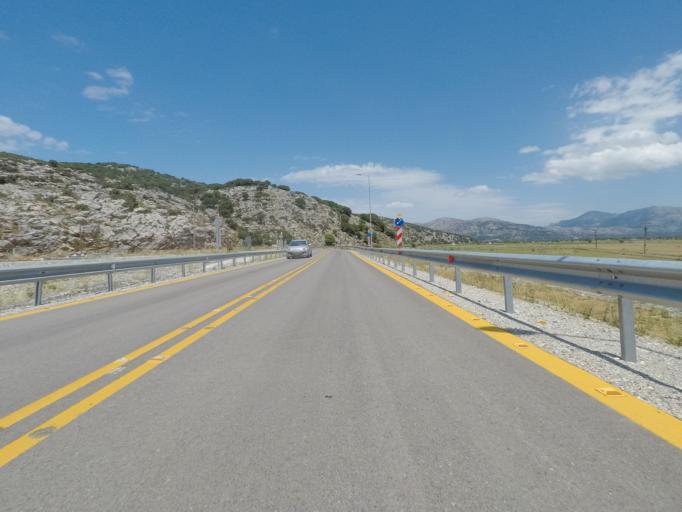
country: GR
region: Crete
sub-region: Nomos Irakleiou
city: Mokhos
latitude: 35.1940
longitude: 25.4437
